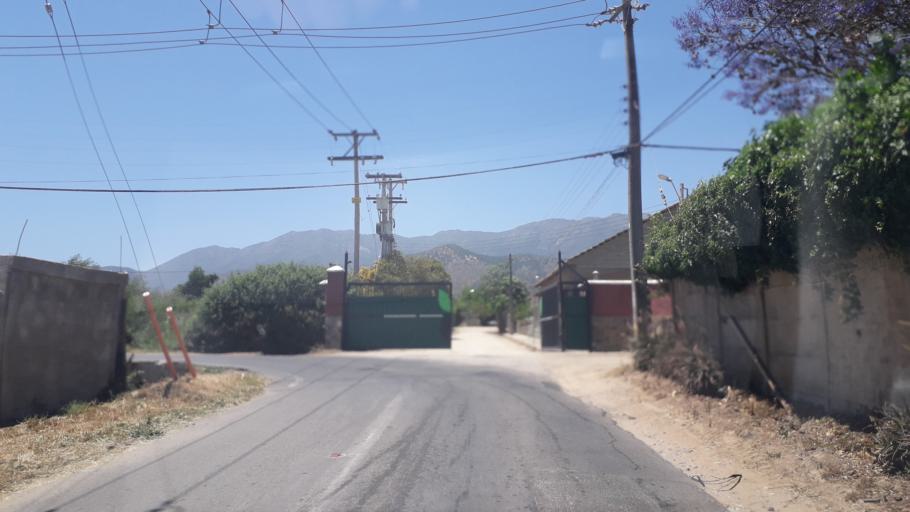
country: CL
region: Valparaiso
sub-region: Provincia de Quillota
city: Quillota
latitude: -32.9080
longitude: -71.2184
